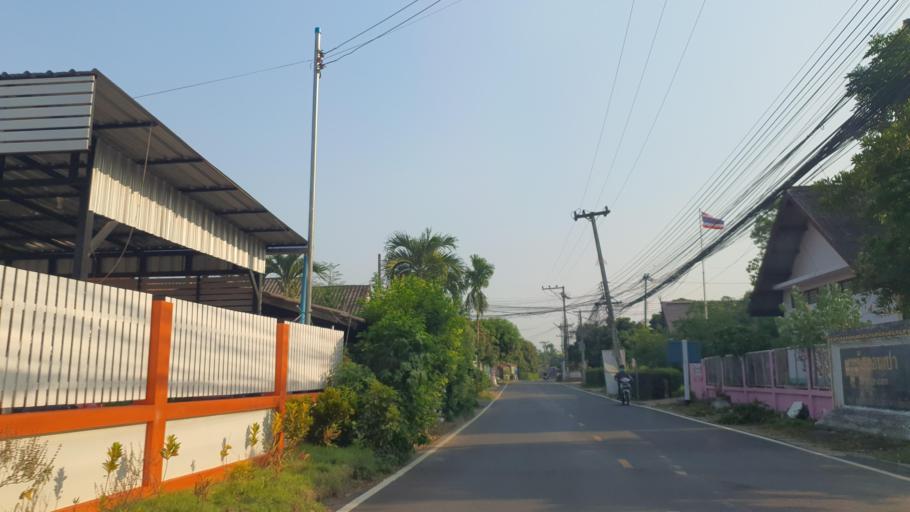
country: TH
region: Chiang Mai
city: Mae Wang
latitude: 18.6060
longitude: 98.8210
